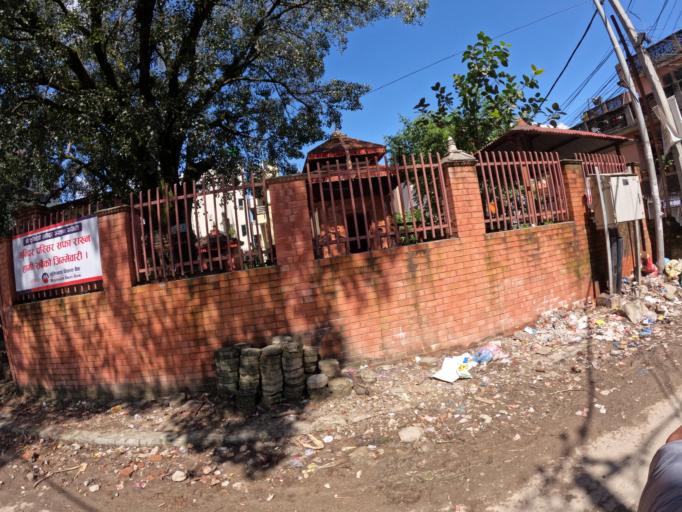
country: NP
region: Central Region
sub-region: Bagmati Zone
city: Kathmandu
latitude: 27.7483
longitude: 85.3312
